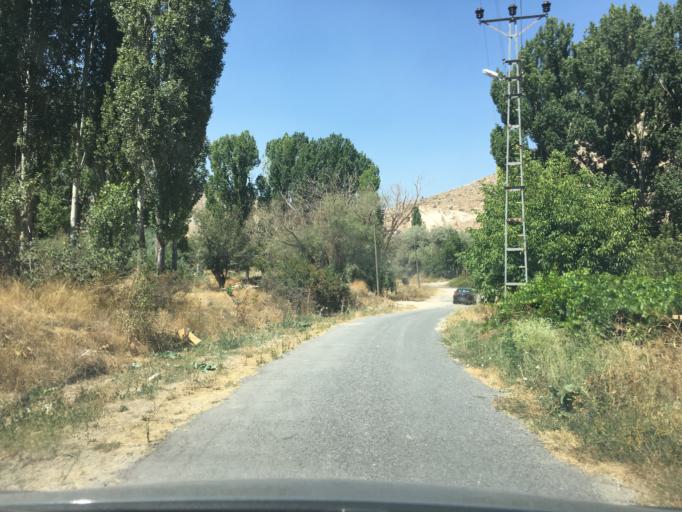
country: TR
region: Nevsehir
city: Urgub
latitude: 38.4694
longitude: 34.9605
